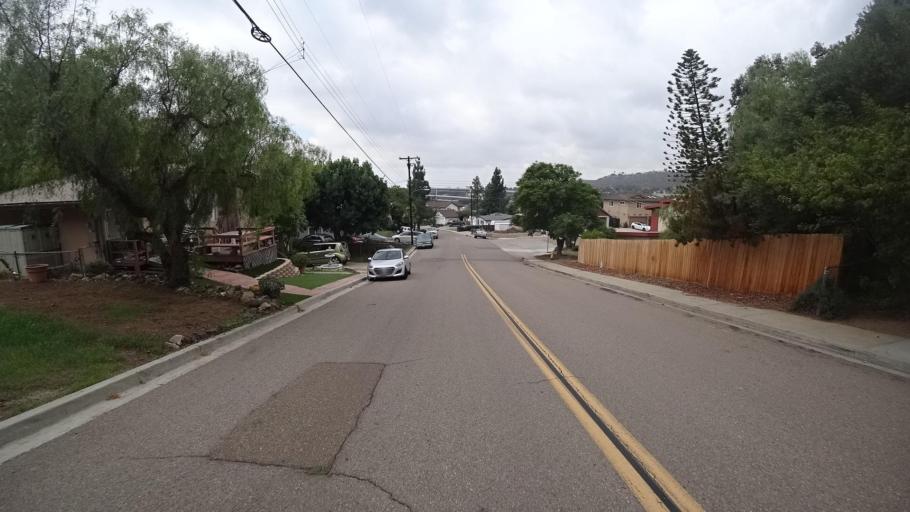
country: US
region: California
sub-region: San Diego County
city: Spring Valley
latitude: 32.7493
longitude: -117.0102
